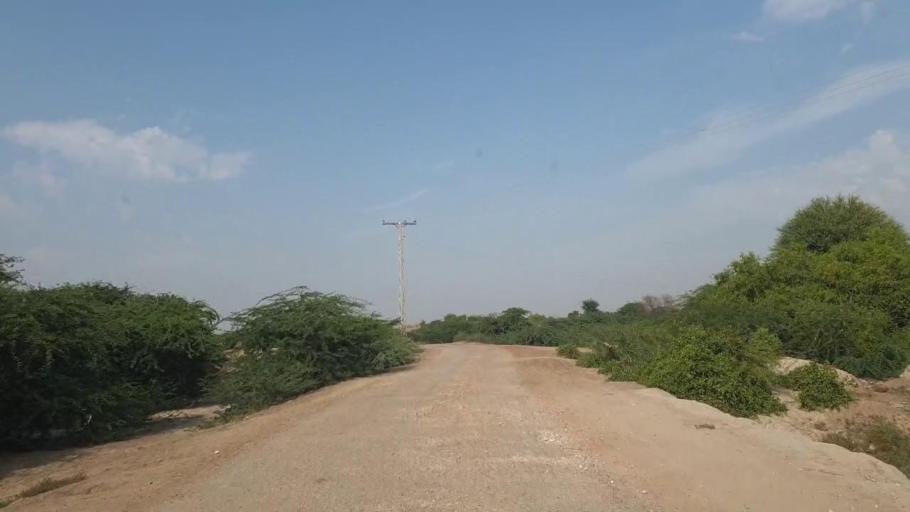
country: PK
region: Sindh
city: Digri
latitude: 25.0057
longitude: 69.0653
